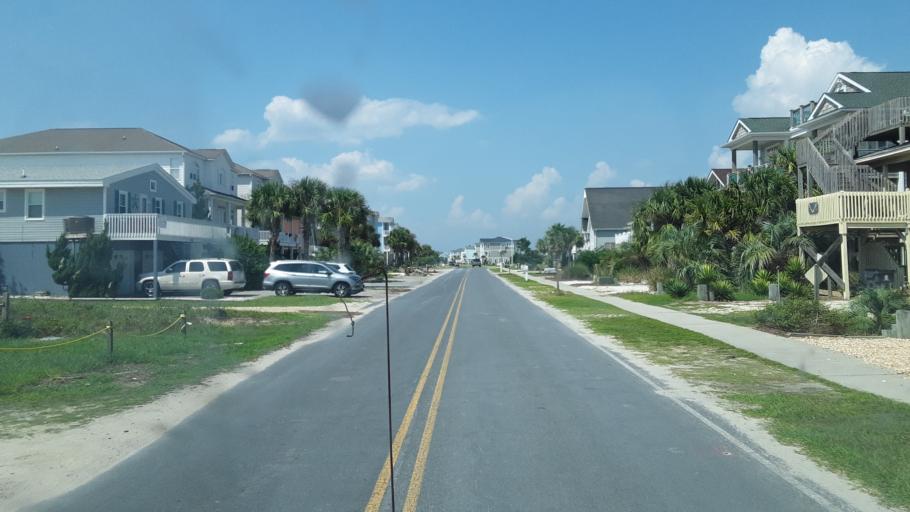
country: US
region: North Carolina
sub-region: Brunswick County
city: Shallotte
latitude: 33.8968
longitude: -78.4000
